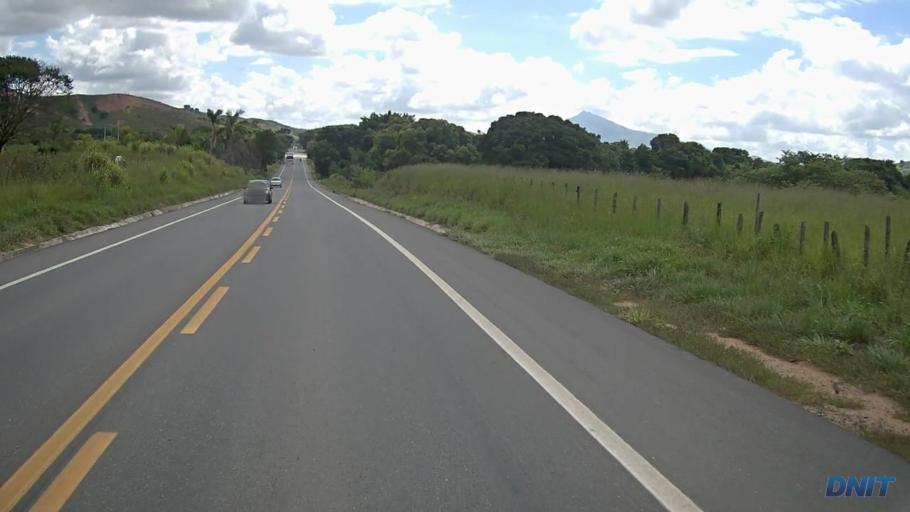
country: BR
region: Minas Gerais
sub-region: Governador Valadares
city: Governador Valadares
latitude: -18.9416
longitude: -42.0590
